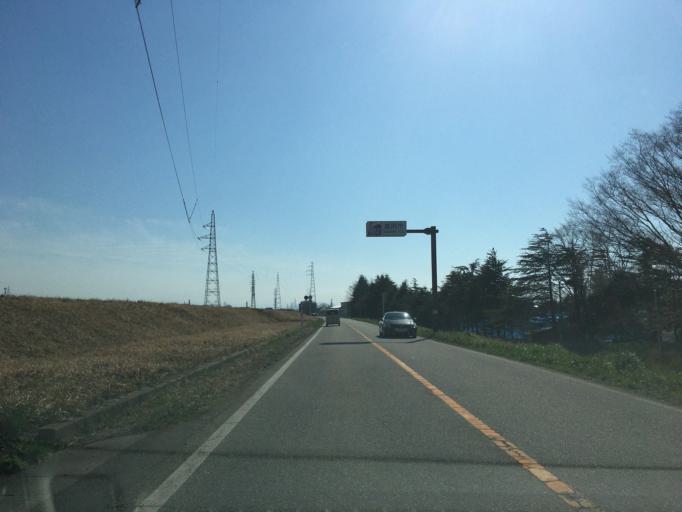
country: JP
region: Toyama
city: Nishishinminato
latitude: 36.7842
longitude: 137.0629
